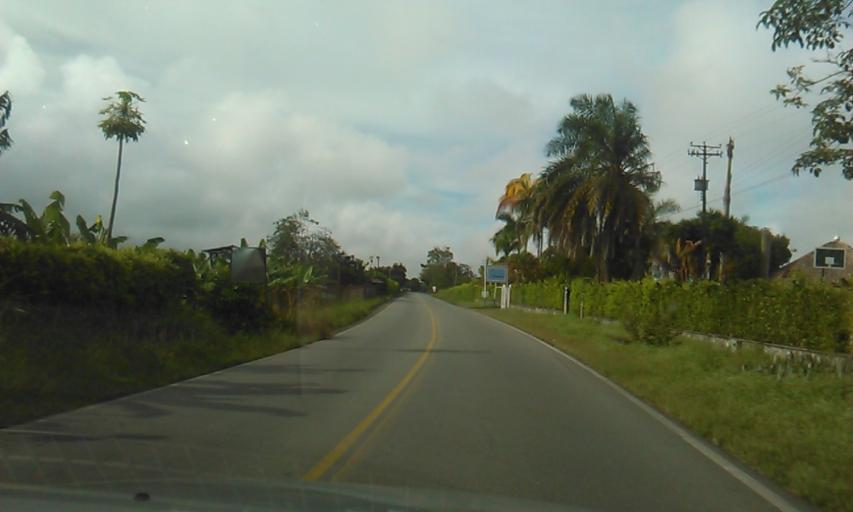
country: CO
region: Quindio
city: Cordoba
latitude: 4.4605
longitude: -75.7103
